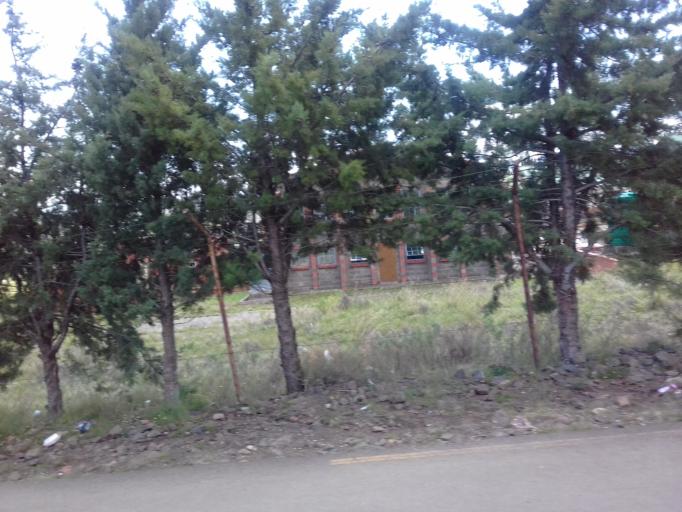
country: LS
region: Thaba-Tseka
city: Thaba-Tseka
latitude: -29.5209
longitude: 28.6076
